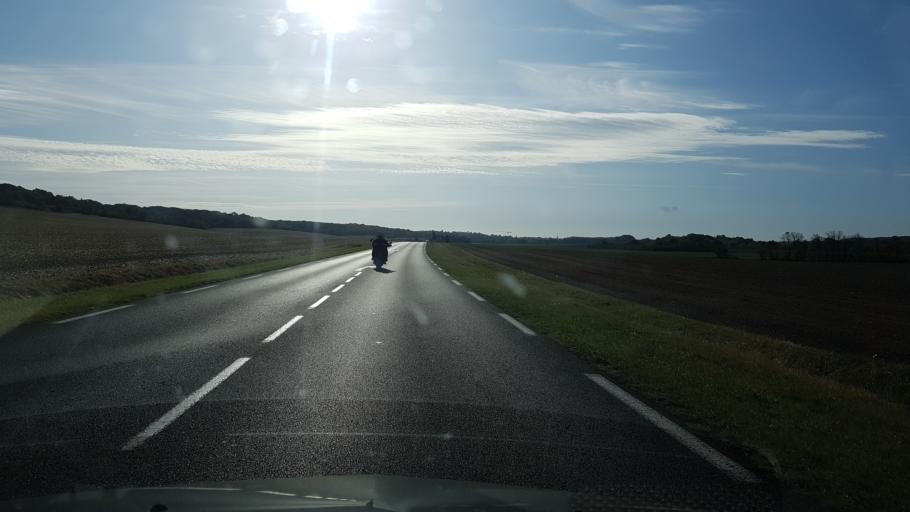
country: FR
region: Centre
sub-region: Departement du Loiret
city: Saint-Brisson-sur-Loire
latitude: 47.6658
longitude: 2.7008
